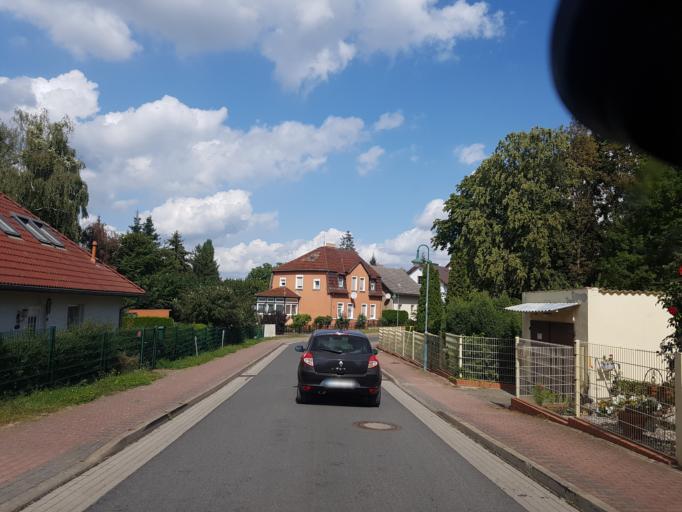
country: DE
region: Brandenburg
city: Gross Kreutz
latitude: 52.3154
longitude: 12.7441
